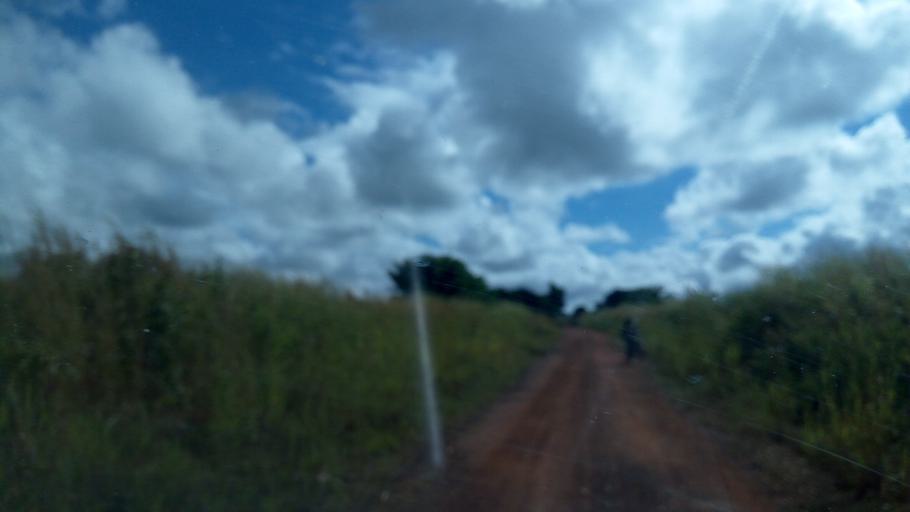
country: ZM
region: Northern
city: Kaputa
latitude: -8.4288
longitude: 28.9247
